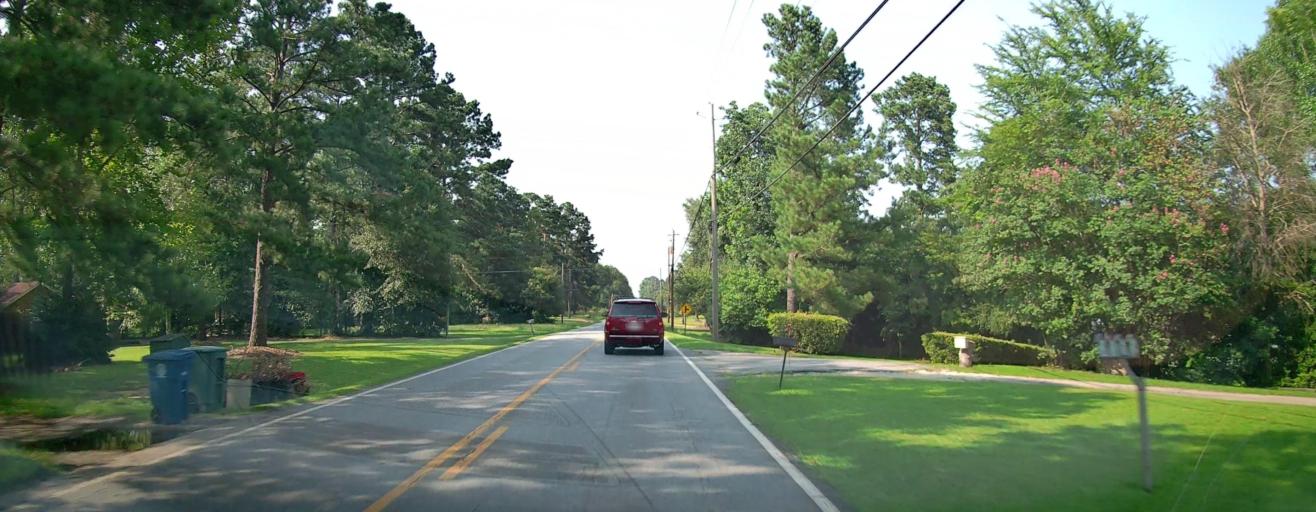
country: US
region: Georgia
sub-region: Houston County
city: Centerville
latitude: 32.7020
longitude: -83.6994
